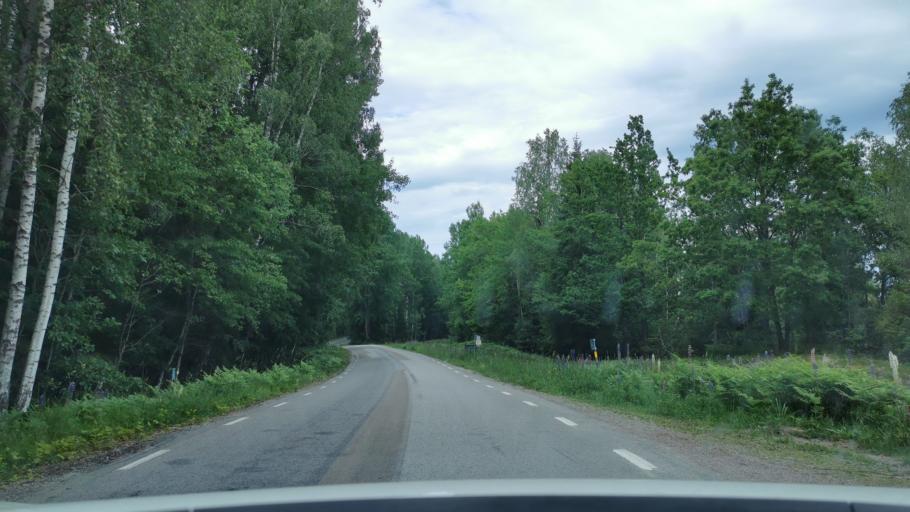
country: SE
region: Vaestra Goetaland
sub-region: Bengtsfors Kommun
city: Dals Langed
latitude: 58.8384
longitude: 12.4103
